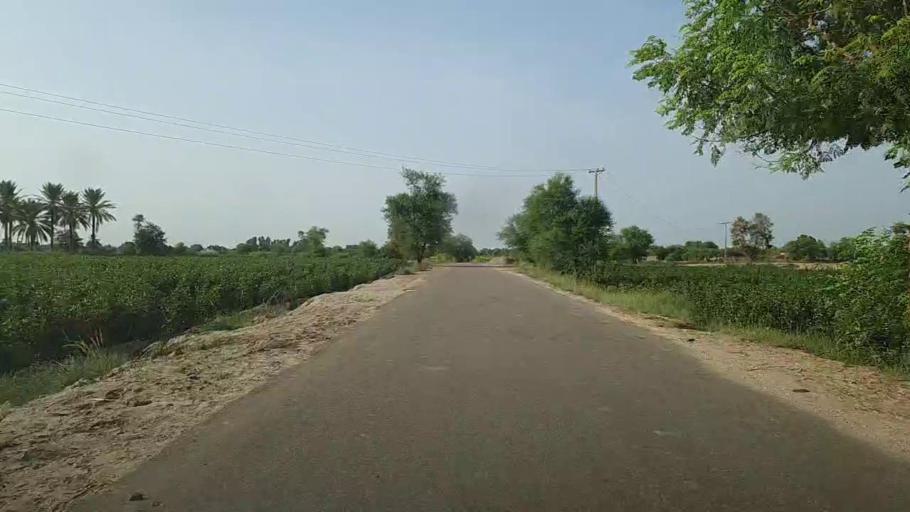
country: PK
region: Sindh
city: Ubauro
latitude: 28.1103
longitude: 69.8498
